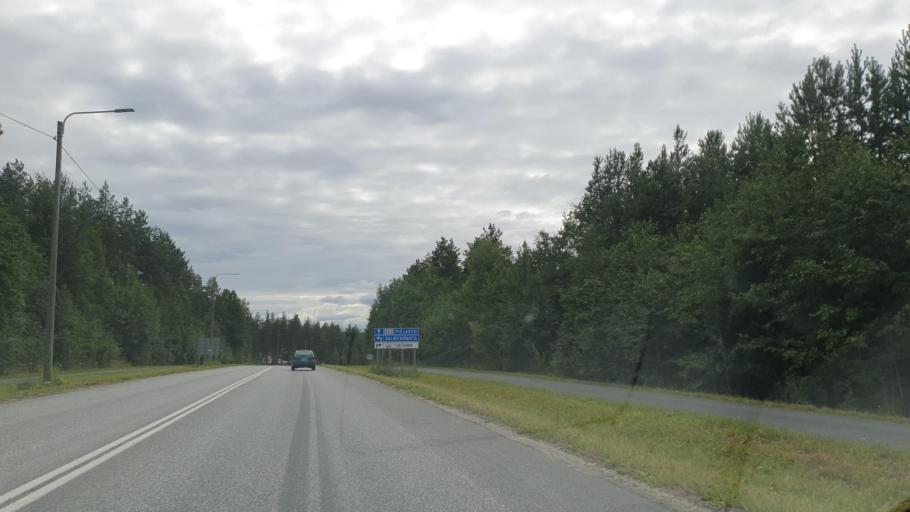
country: FI
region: Northern Savo
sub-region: Ylae-Savo
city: Iisalmi
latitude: 63.5214
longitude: 27.2413
